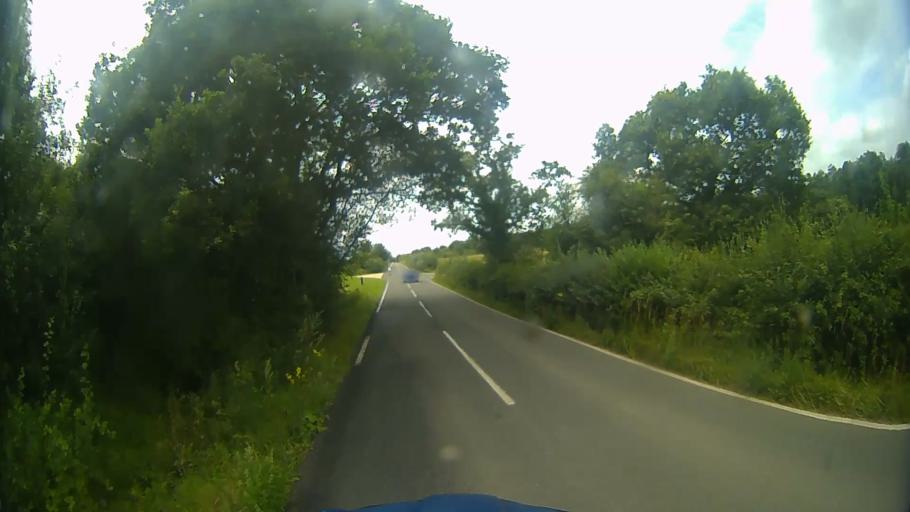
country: GB
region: England
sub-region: Hampshire
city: Kingsley
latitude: 51.1722
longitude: -0.8646
